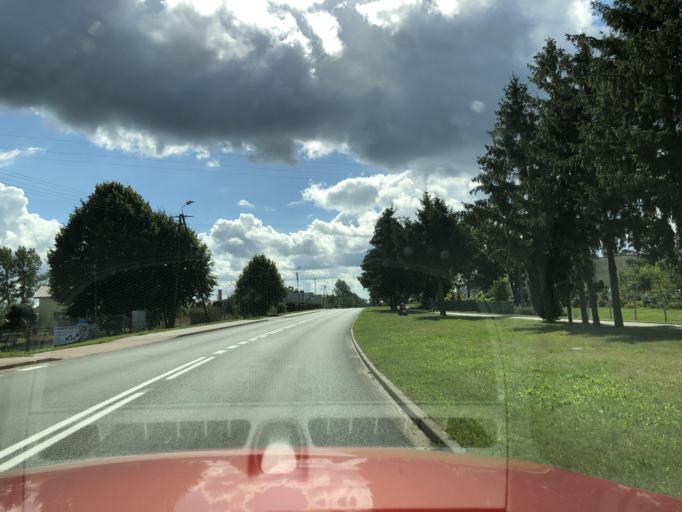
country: PL
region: West Pomeranian Voivodeship
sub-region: Powiat szczecinecki
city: Bialy Bor
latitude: 53.8296
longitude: 16.8394
